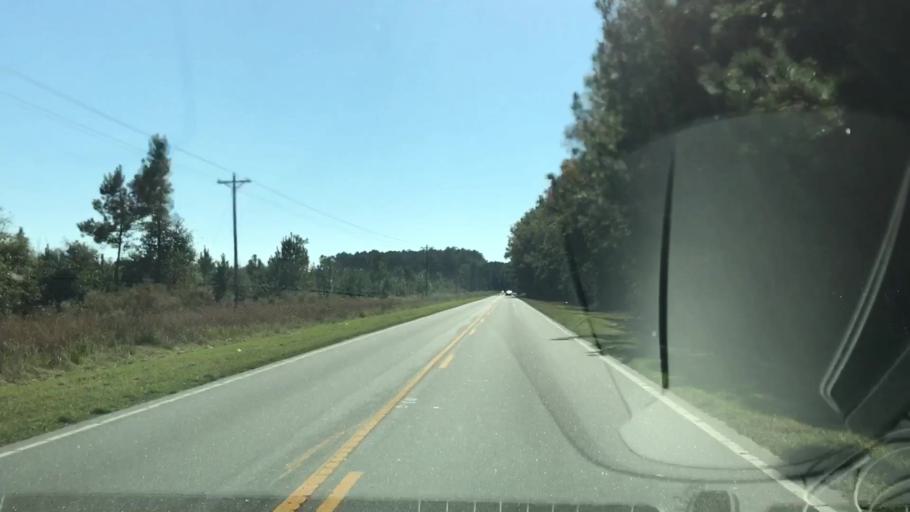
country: US
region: South Carolina
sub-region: Jasper County
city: Ridgeland
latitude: 32.4448
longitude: -80.8960
